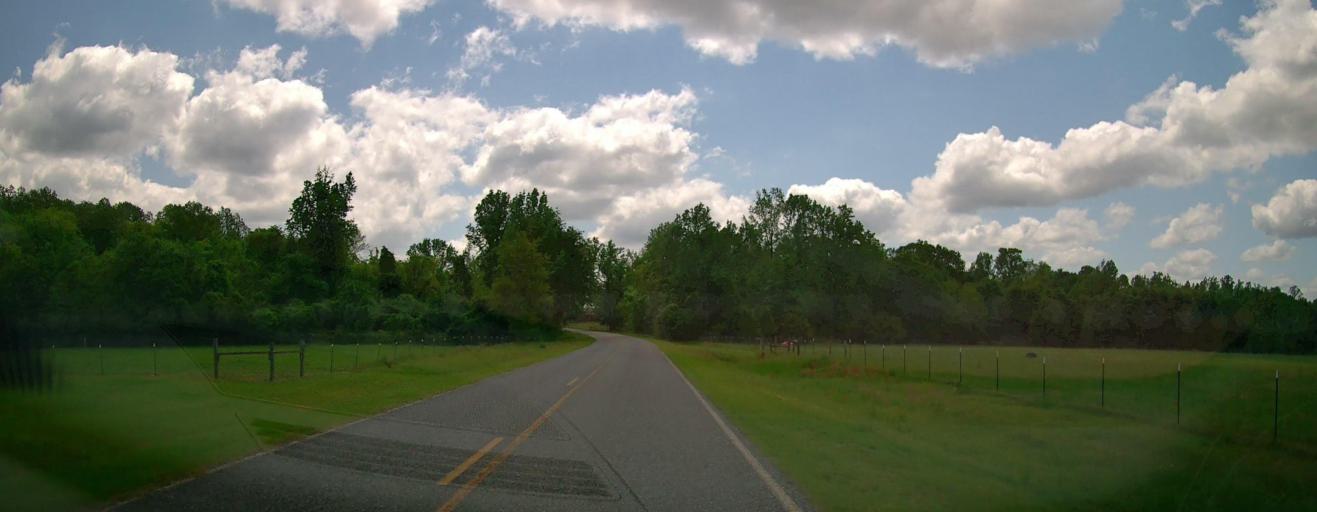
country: US
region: Georgia
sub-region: Dodge County
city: Chester
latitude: 32.5511
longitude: -83.1451
